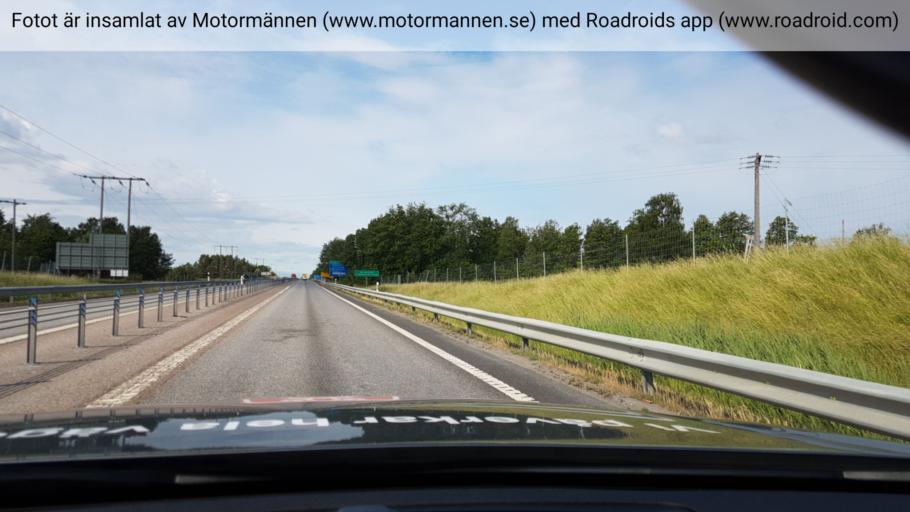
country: SE
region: Vaestmanland
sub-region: Hallstahammars Kommun
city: Hallstahammar
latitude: 59.5915
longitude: 16.2358
